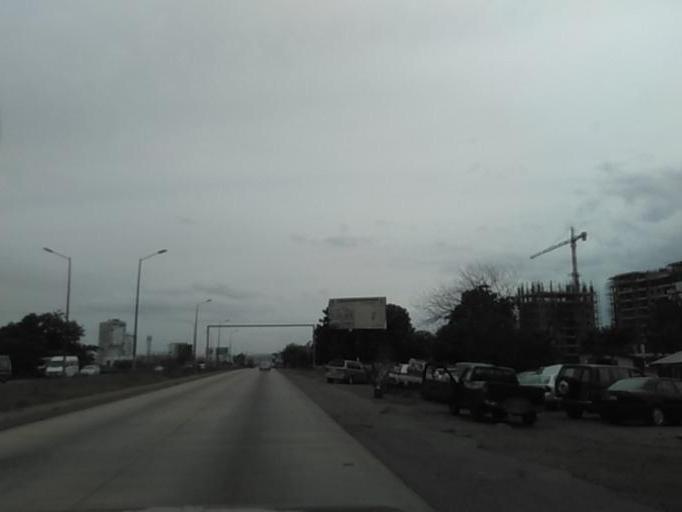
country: GH
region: Greater Accra
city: Medina Estates
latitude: 5.6254
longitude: -0.1696
